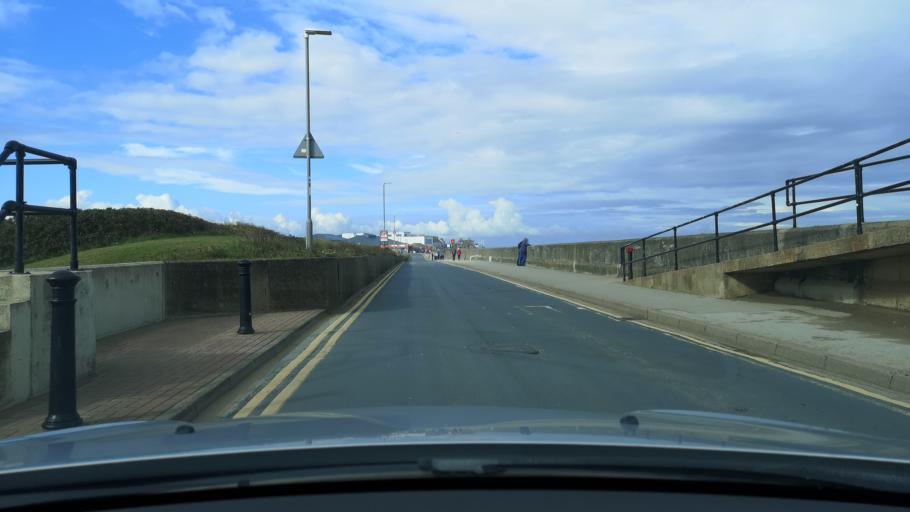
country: GB
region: England
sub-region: East Riding of Yorkshire
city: Hornsea
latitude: 53.9094
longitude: -0.1587
